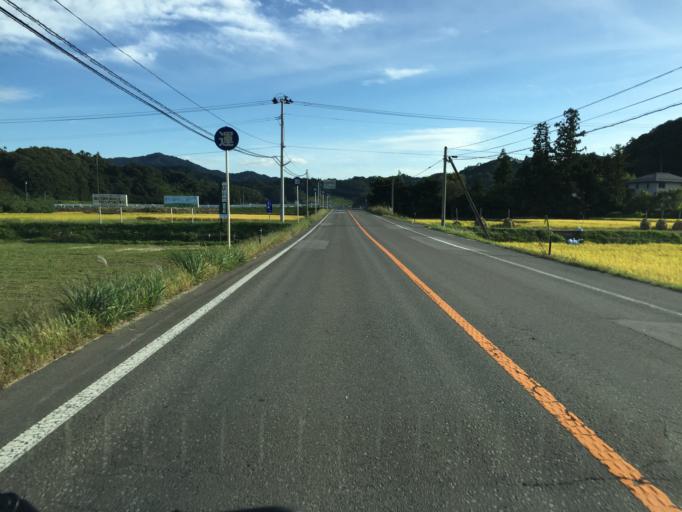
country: JP
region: Fukushima
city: Hobaramachi
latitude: 37.7519
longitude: 140.6069
